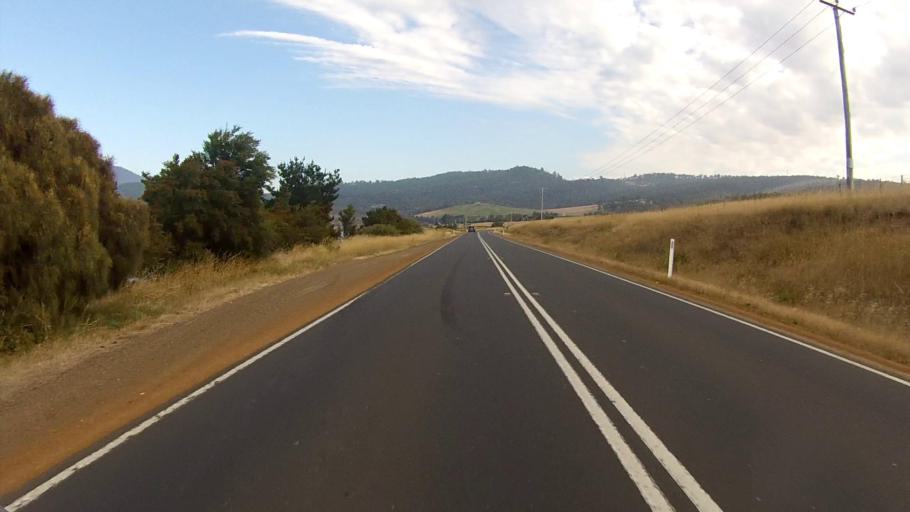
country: AU
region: Tasmania
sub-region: Brighton
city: Bridgewater
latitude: -42.7350
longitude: 147.2128
